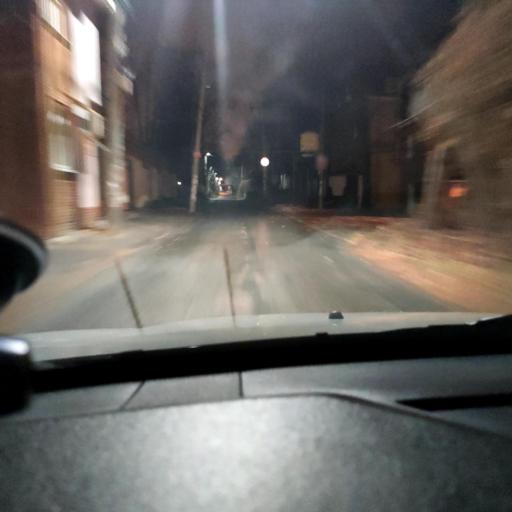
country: RU
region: Samara
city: Samara
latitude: 53.2986
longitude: 50.2010
